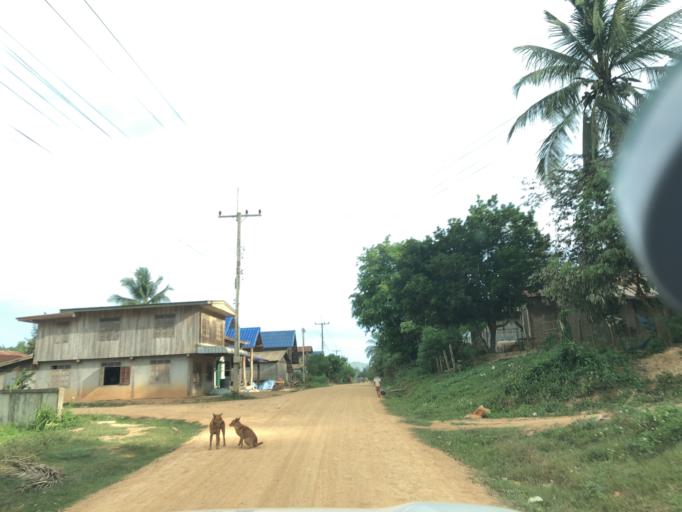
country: TH
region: Loei
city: Chiang Khan
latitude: 18.0181
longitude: 101.4190
